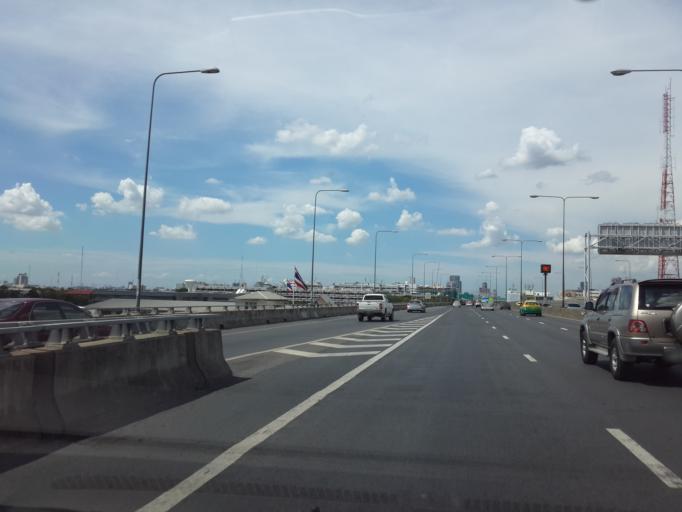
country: TH
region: Bangkok
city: Ratchathewi
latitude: 13.7594
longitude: 100.5247
